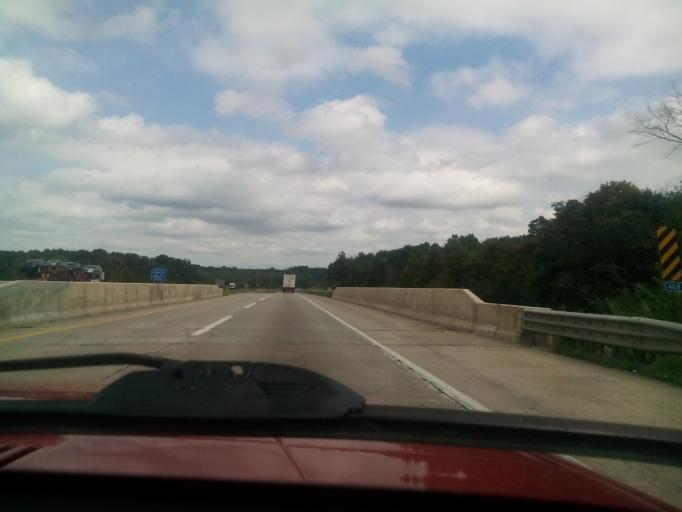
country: US
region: Indiana
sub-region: LaPorte County
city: Westville
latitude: 41.5996
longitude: -86.8649
